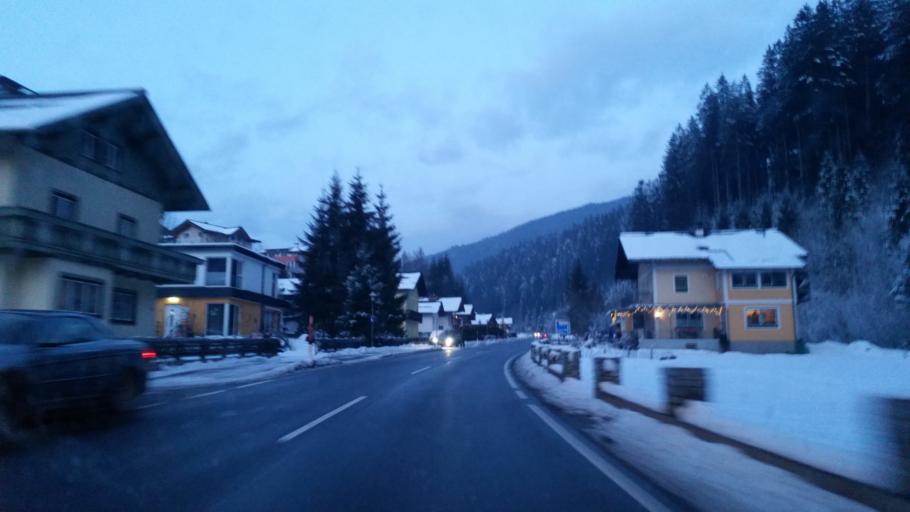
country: AT
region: Salzburg
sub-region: Politischer Bezirk Sankt Johann im Pongau
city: Huttau
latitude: 47.4274
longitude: 13.3490
